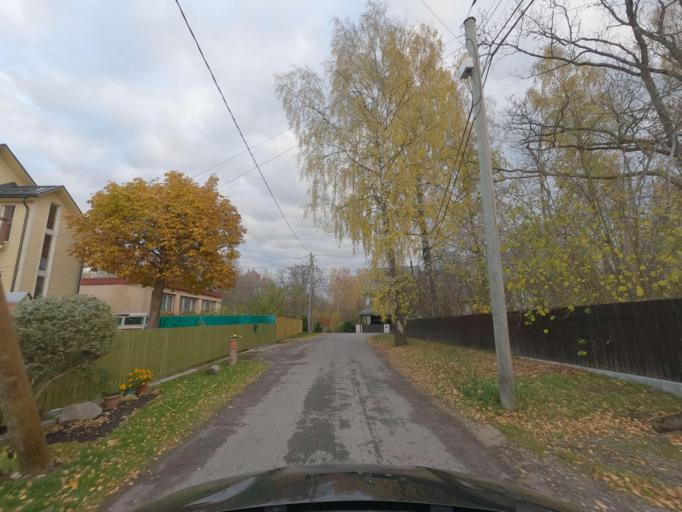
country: EE
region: Harju
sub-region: Saue linn
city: Saue
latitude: 59.3167
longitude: 24.5447
